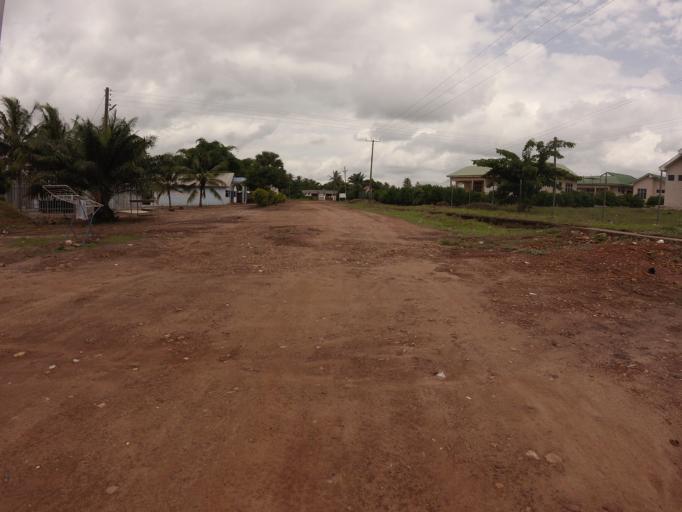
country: GH
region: Volta
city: Ho
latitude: 6.5976
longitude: 0.4853
